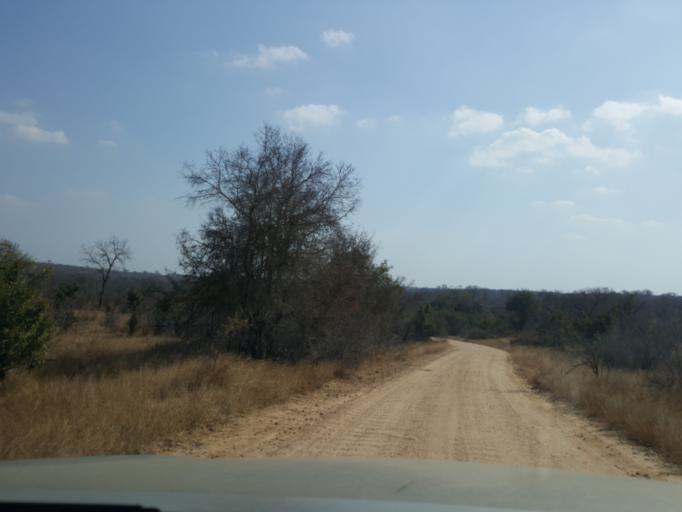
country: ZA
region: Mpumalanga
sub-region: Ehlanzeni District
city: Komatipoort
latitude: -25.2730
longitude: 31.7832
